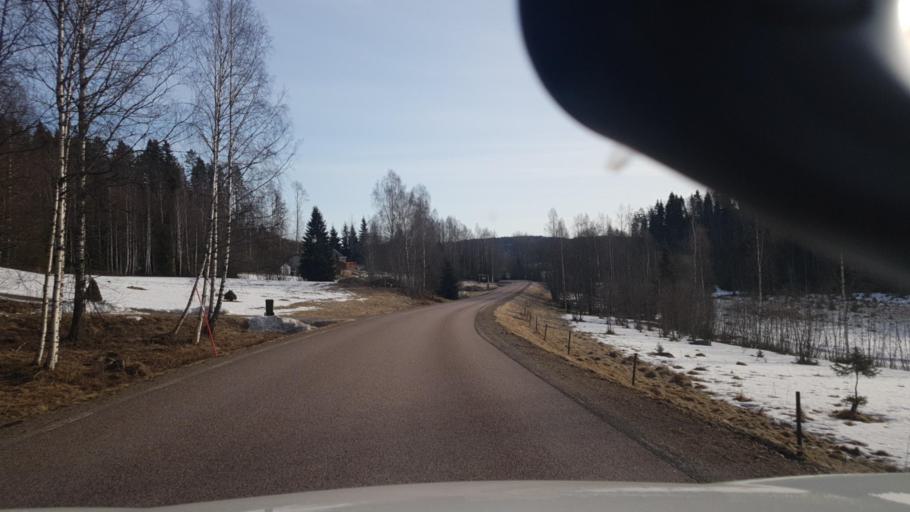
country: SE
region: Vaermland
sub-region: Eda Kommun
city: Amotfors
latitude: 59.8745
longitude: 12.5055
